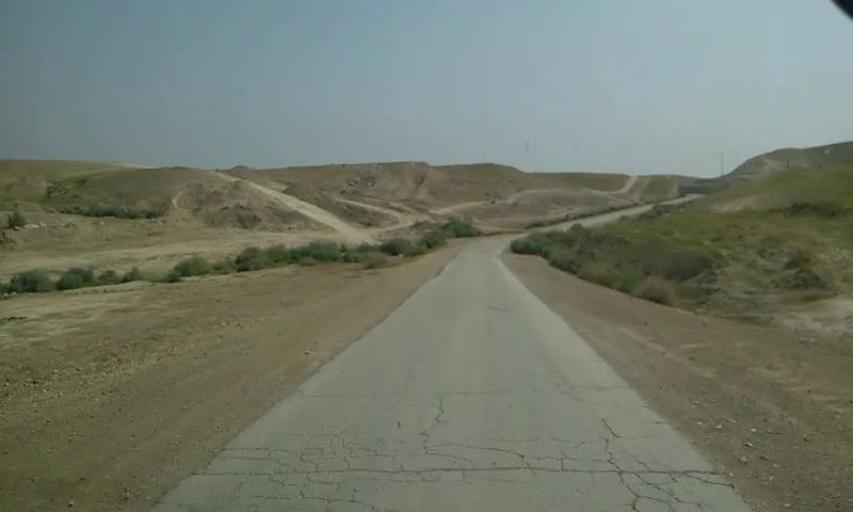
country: PS
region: West Bank
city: Jericho
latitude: 31.7951
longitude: 35.4269
